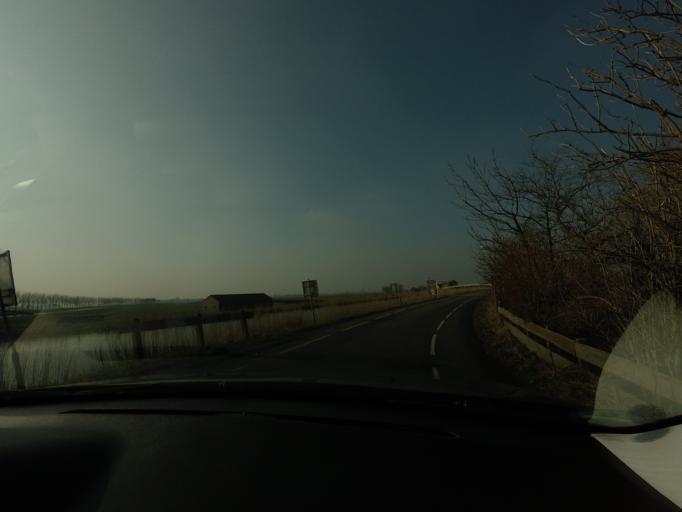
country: NL
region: North Holland
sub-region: Gemeente Beemster
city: Halfweg
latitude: 52.6137
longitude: 4.9477
